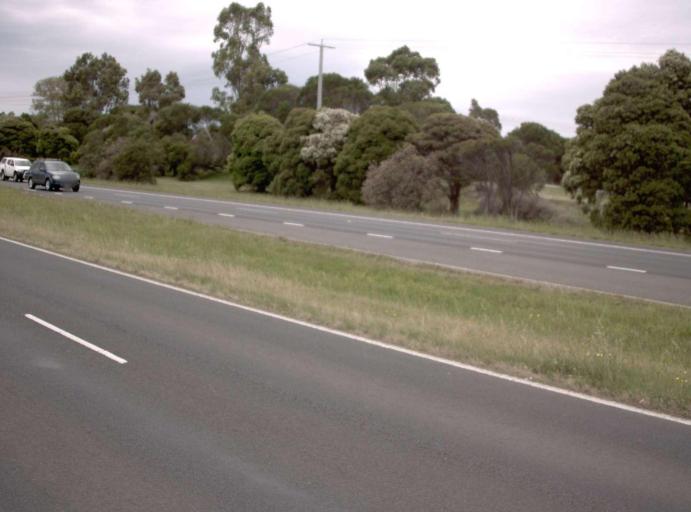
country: AU
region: Victoria
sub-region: Casey
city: Cranbourne North
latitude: -38.0855
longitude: 145.2781
